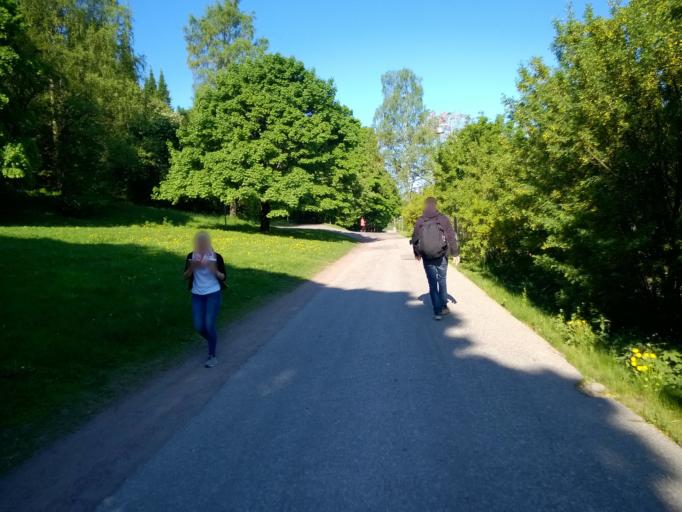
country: FI
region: Uusimaa
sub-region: Helsinki
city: Helsinki
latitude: 60.1991
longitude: 24.9592
